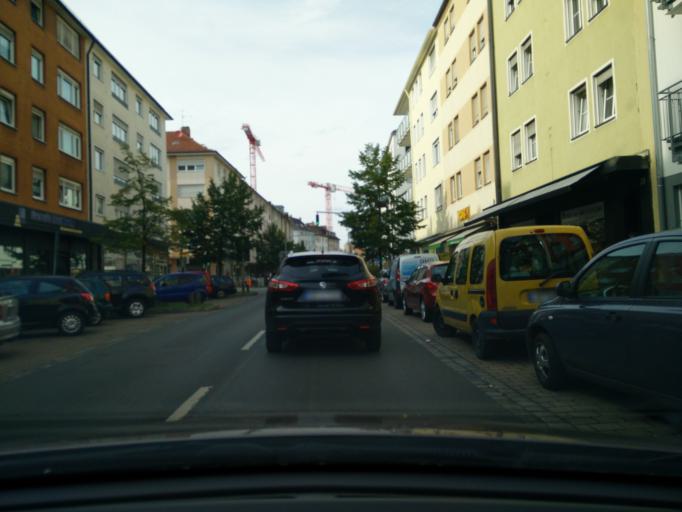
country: DE
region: Bavaria
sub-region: Regierungsbezirk Mittelfranken
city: Nuernberg
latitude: 49.4411
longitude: 11.0761
